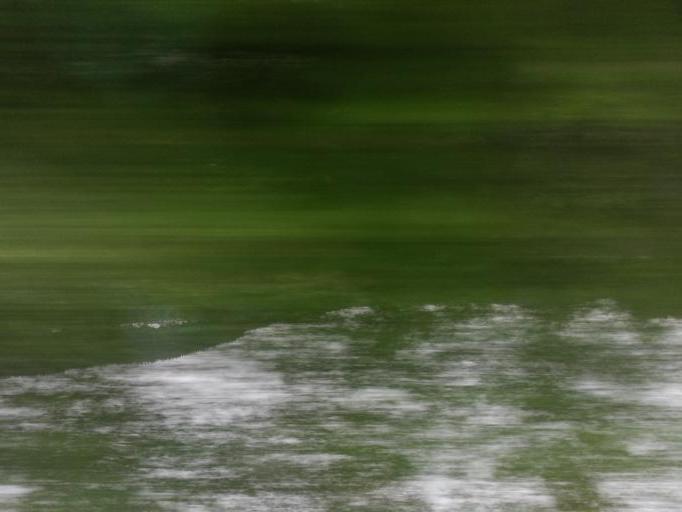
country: NO
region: Sor-Trondelag
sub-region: Melhus
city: Melhus
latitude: 63.2789
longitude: 10.2840
